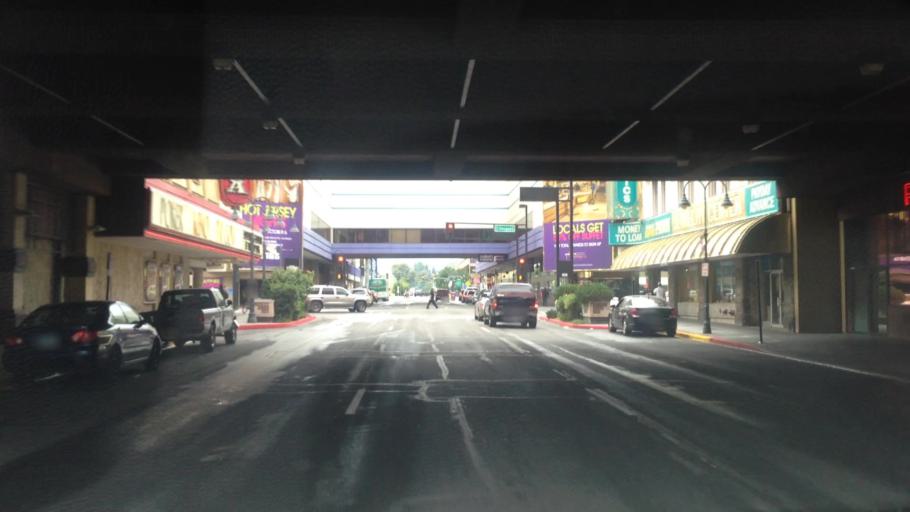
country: US
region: Nevada
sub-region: Washoe County
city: Reno
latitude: 39.5266
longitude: -119.8118
